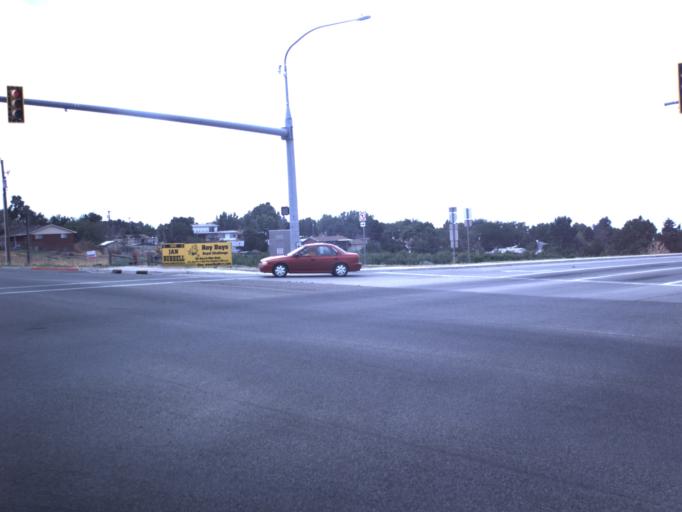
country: US
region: Utah
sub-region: Weber County
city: West Haven
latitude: 41.1982
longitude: -112.0258
